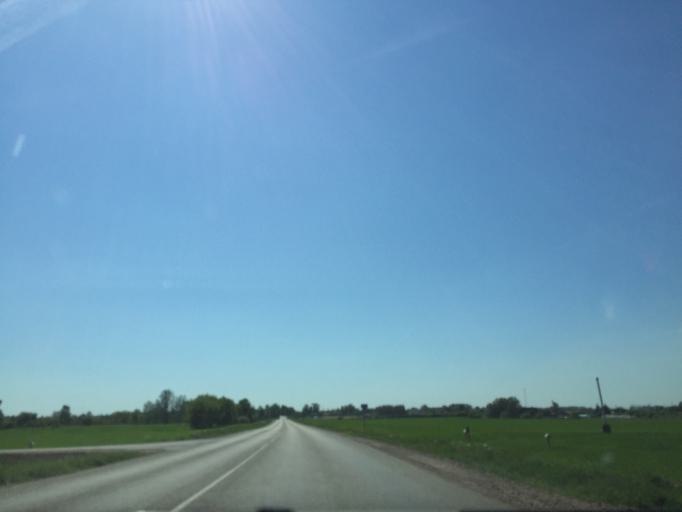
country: LV
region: Bauskas Rajons
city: Bauska
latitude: 56.4256
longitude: 24.2274
